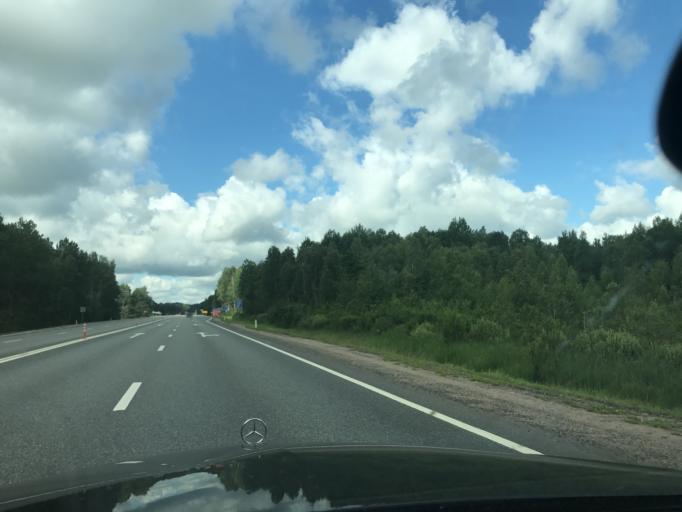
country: RU
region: Smolensk
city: Golynki
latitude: 54.7056
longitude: 31.2151
